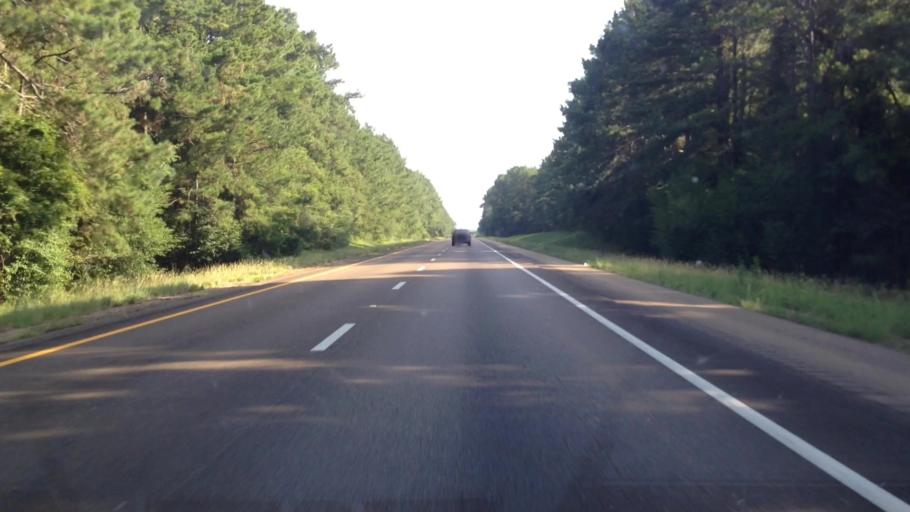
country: US
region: Mississippi
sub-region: Pike County
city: Summit
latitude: 31.3401
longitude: -90.4778
